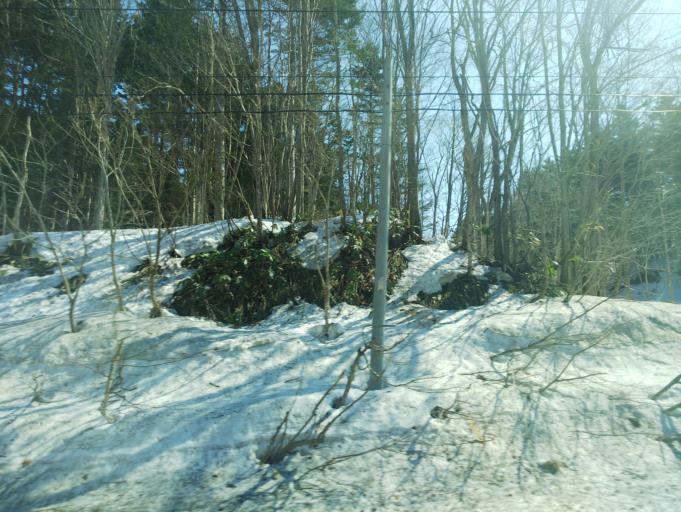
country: JP
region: Hokkaido
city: Nayoro
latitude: 44.7126
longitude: 142.2738
